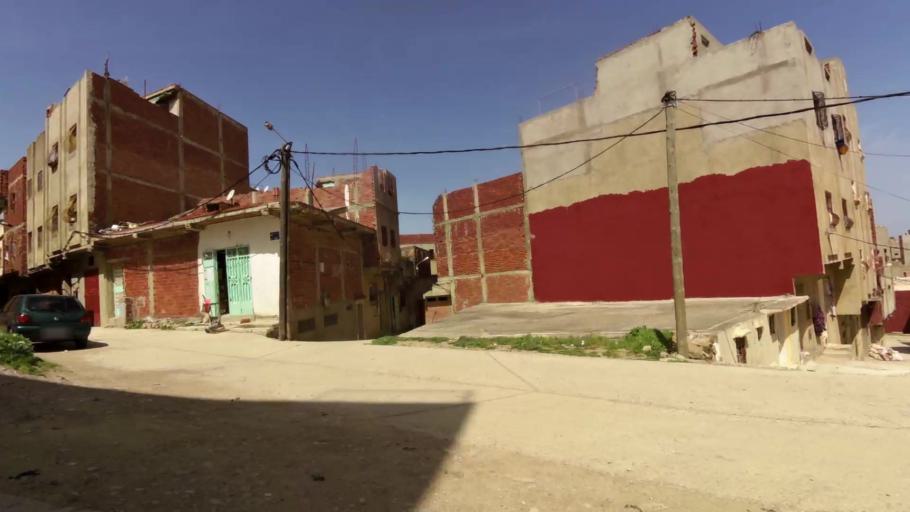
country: MA
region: Tanger-Tetouan
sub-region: Tanger-Assilah
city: Tangier
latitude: 35.7312
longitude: -5.8107
